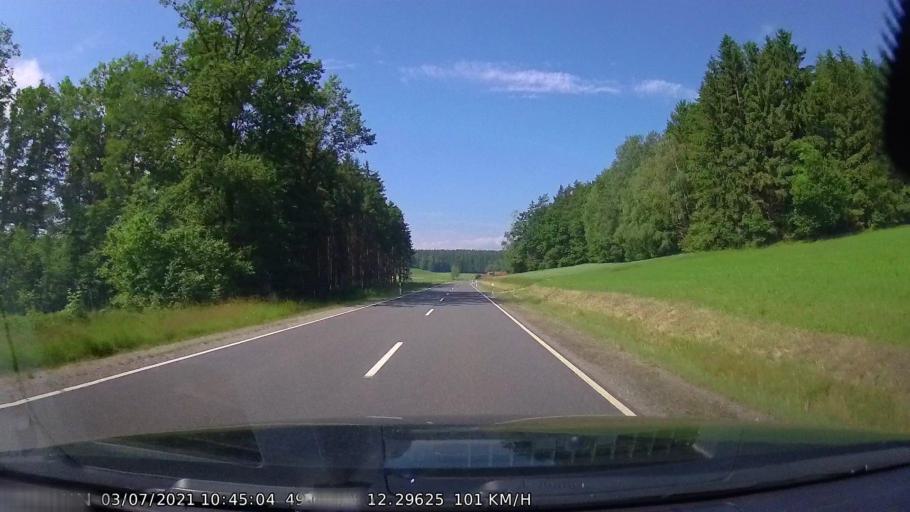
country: DE
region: Bavaria
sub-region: Upper Palatinate
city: Leuchtenberg
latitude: 49.6068
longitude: 12.2963
